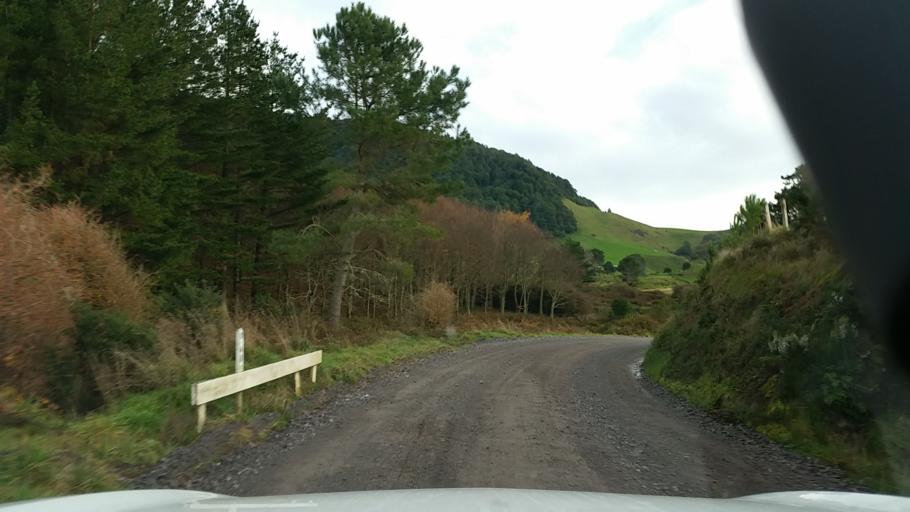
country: NZ
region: Bay of Plenty
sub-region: Rotorua District
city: Rotorua
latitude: -38.2356
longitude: 176.1655
